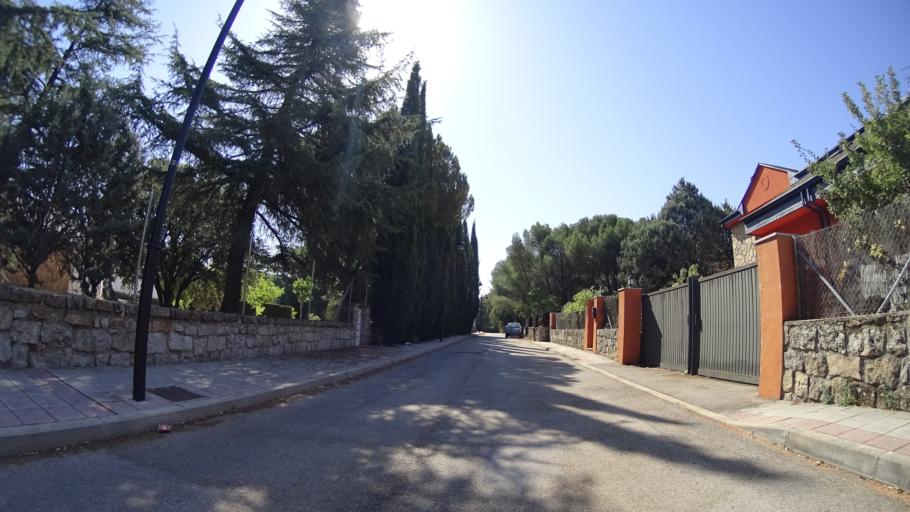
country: ES
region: Madrid
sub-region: Provincia de Madrid
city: Galapagar
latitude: 40.5944
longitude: -3.9828
